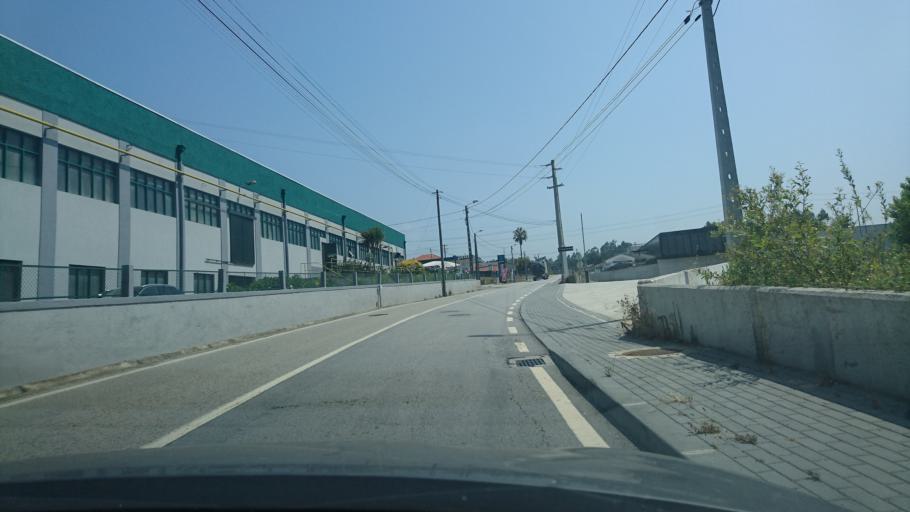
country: PT
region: Aveiro
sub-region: Espinho
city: Souto
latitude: 40.9789
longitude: -8.6036
